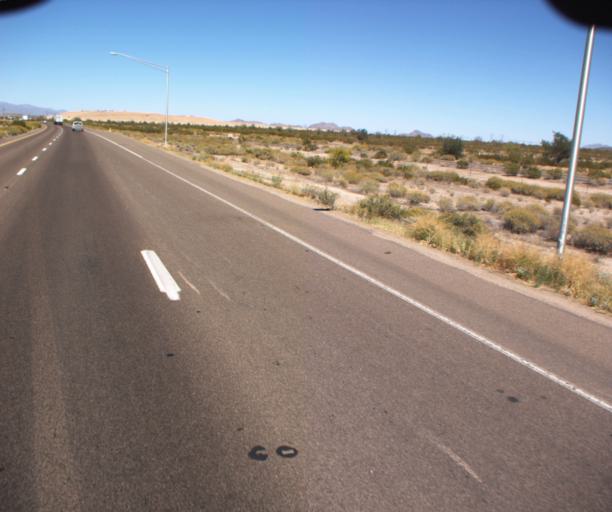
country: US
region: Arizona
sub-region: Maricopa County
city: Buckeye
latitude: 33.2030
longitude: -112.6475
